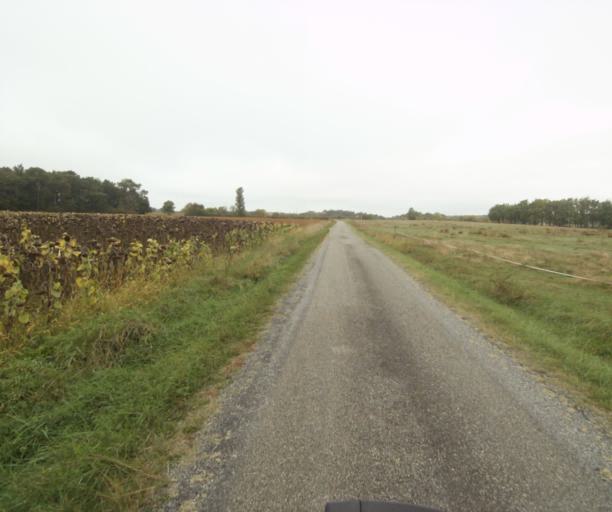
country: FR
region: Midi-Pyrenees
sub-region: Departement du Tarn-et-Garonne
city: Orgueil
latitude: 43.8982
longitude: 1.3889
